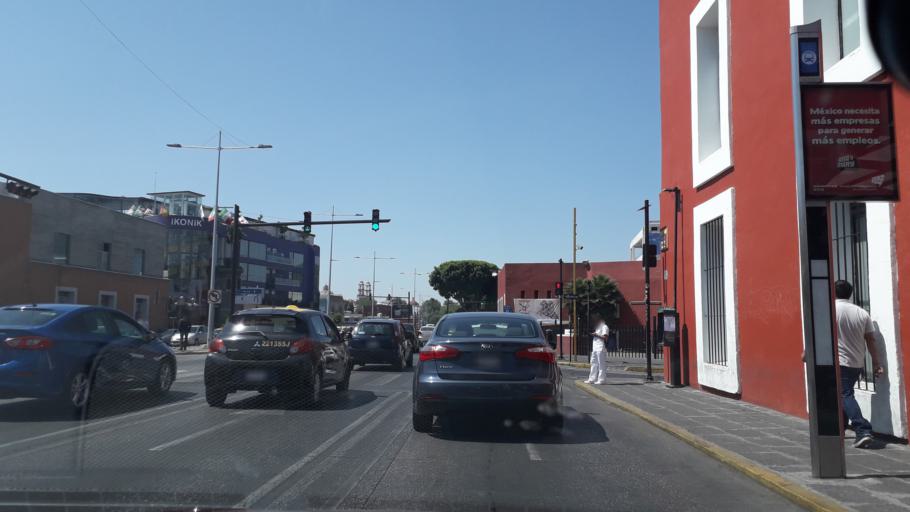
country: MX
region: Puebla
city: Puebla
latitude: 19.0434
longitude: -98.1923
